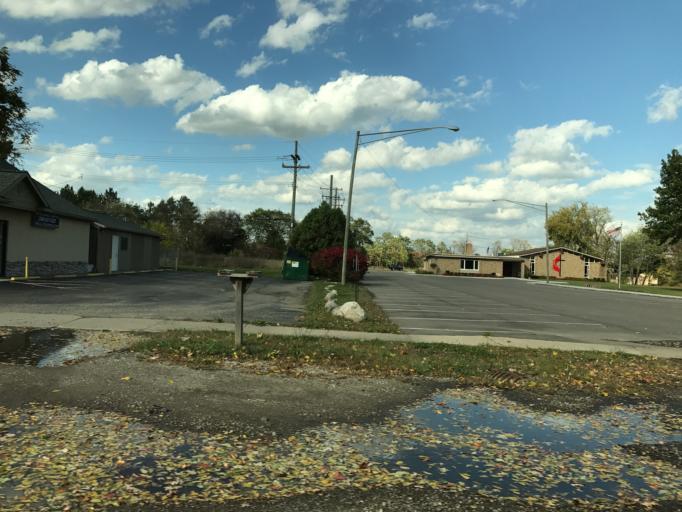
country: US
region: Michigan
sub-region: Oakland County
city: South Lyon
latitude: 42.5110
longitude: -83.6127
